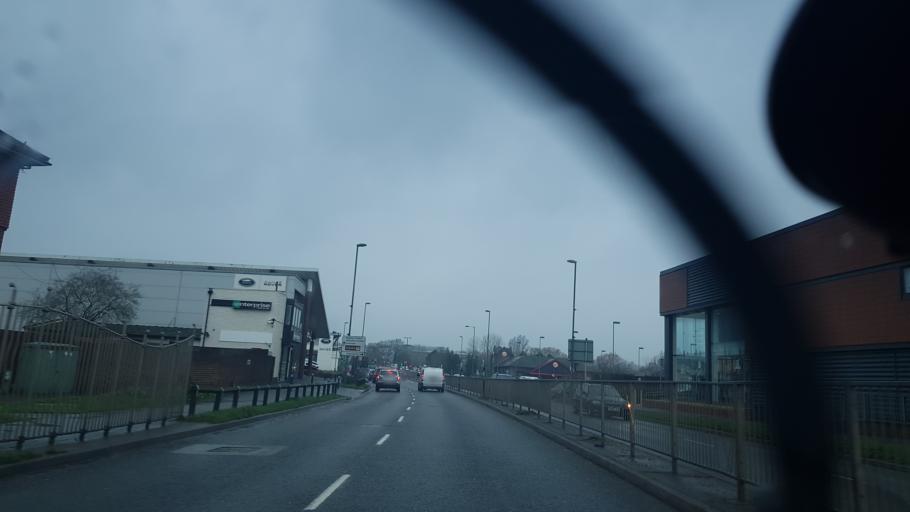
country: GB
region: England
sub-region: Surrey
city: Guildford
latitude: 51.2481
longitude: -0.5766
